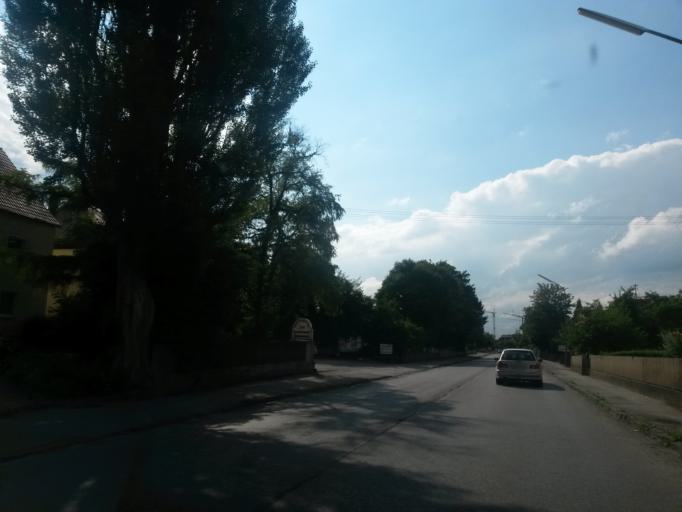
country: DE
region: Bavaria
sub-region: Upper Bavaria
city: Fahrenzhausen
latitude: 48.3509
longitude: 11.5625
